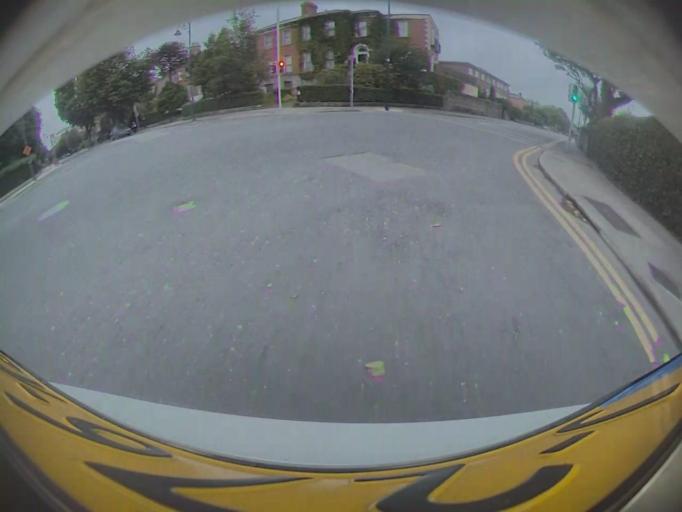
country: IE
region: Leinster
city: Ringsend
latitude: 53.3339
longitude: -6.2318
